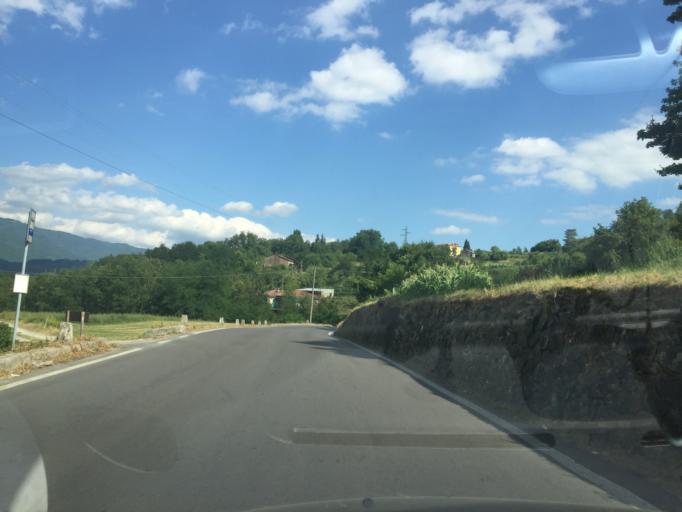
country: IT
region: Tuscany
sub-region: Provincia di Lucca
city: Pieve Fosciana
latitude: 44.1302
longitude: 10.3764
